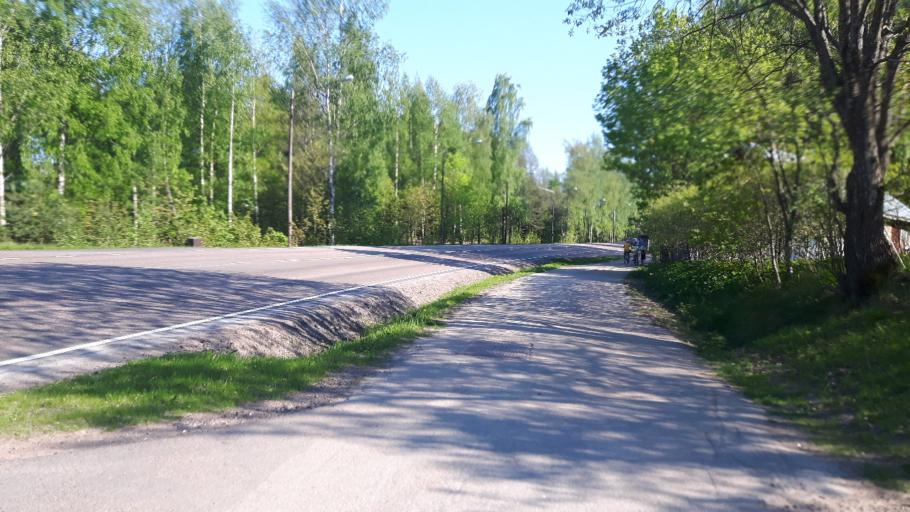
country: FI
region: Kymenlaakso
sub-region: Kotka-Hamina
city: Kotka
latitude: 60.4529
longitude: 26.8937
